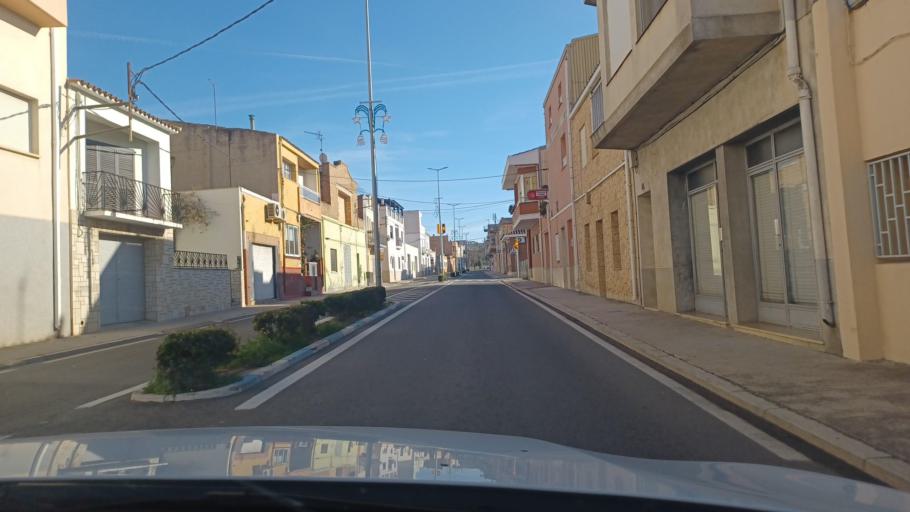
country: ES
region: Catalonia
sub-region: Provincia de Tarragona
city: Masdenverge
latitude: 40.7145
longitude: 0.5305
